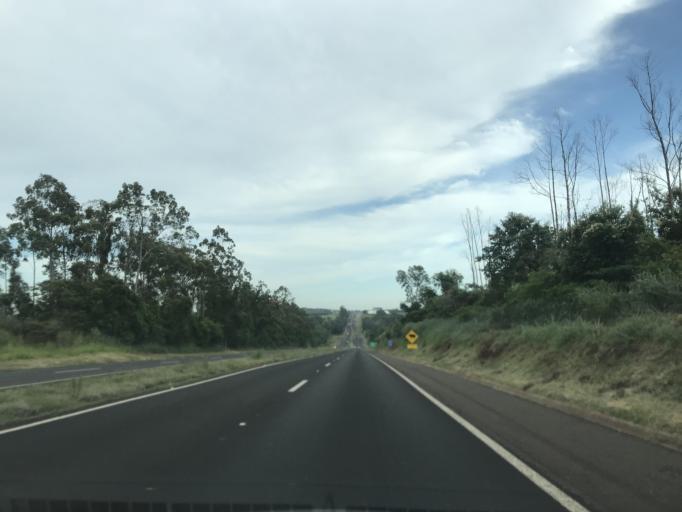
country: BR
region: Parana
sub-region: Alto Parana
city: Alto Parana
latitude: -23.1437
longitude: -52.2821
